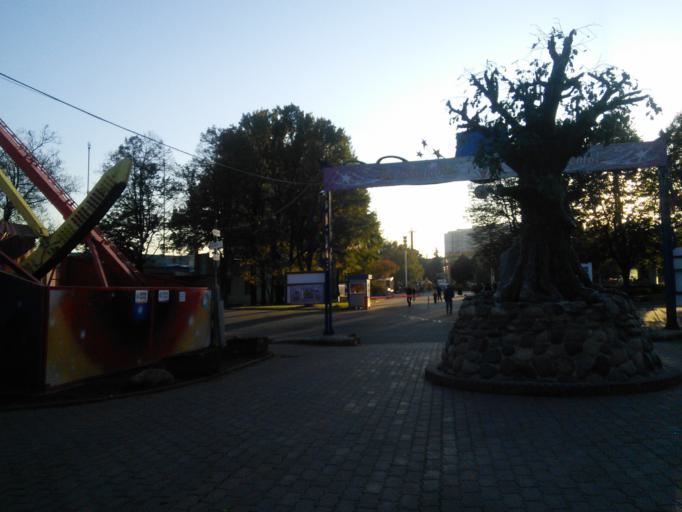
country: RU
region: Moscow
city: Ostankinskiy
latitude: 55.8273
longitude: 37.6389
